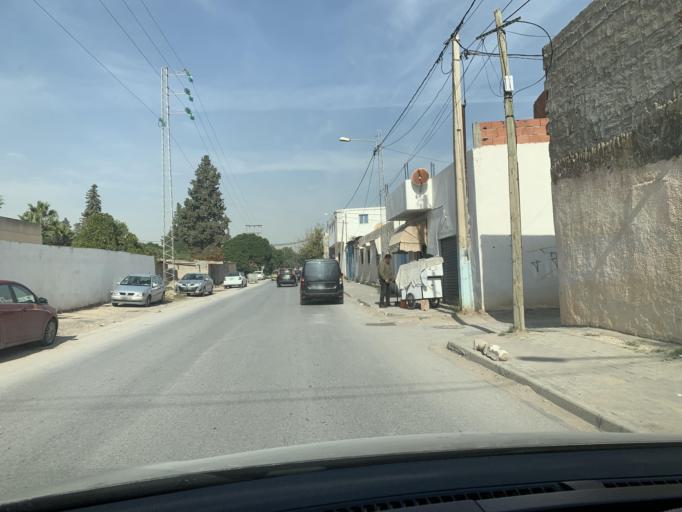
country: TN
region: Manouba
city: Manouba
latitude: 36.8133
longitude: 10.1171
